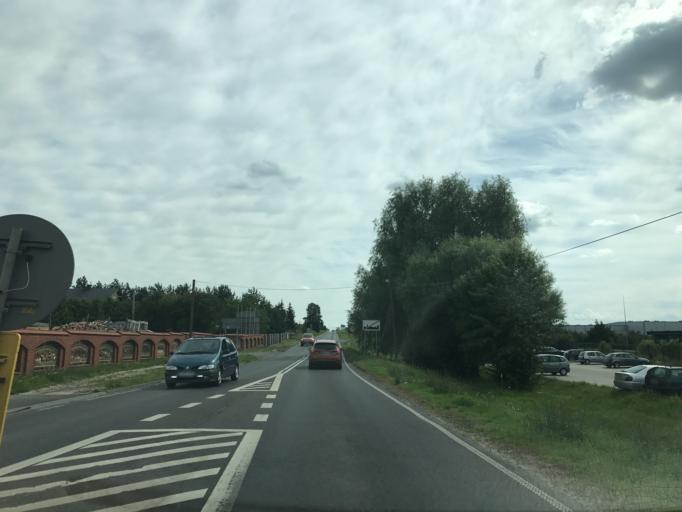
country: PL
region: Kujawsko-Pomorskie
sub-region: Powiat brodnicki
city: Brodnica
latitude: 53.2287
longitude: 19.3880
